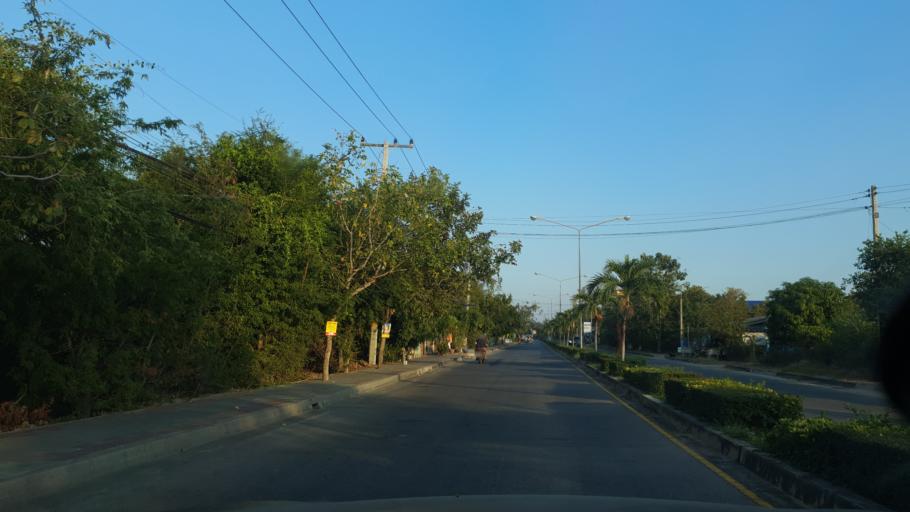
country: TH
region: Phetchaburi
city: Cha-am
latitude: 12.7801
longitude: 99.9700
